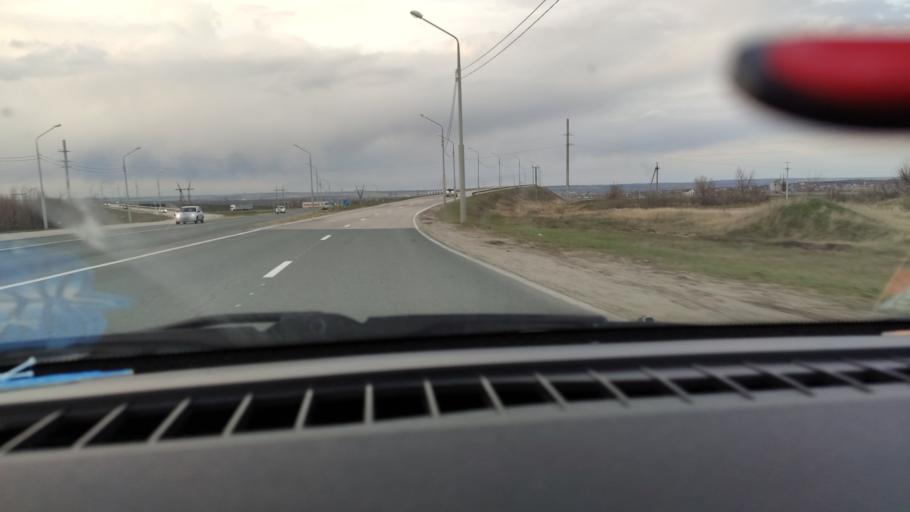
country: RU
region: Saratov
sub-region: Saratovskiy Rayon
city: Saratov
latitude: 51.6695
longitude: 46.0015
